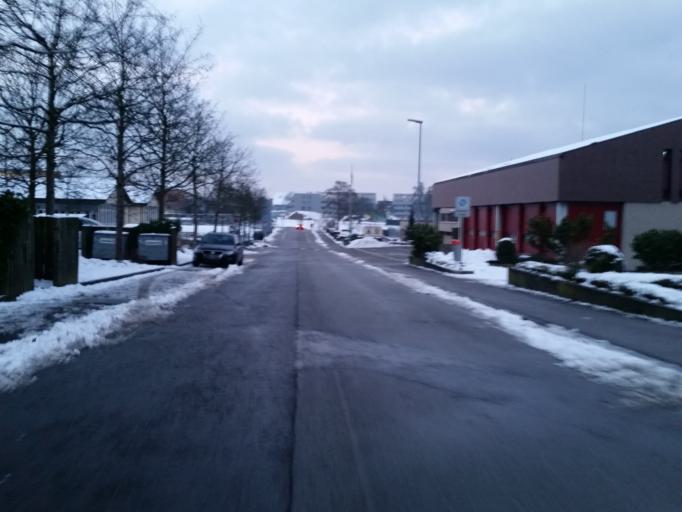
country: CH
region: Thurgau
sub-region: Arbon District
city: Romanshorn
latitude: 47.5665
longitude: 9.3739
